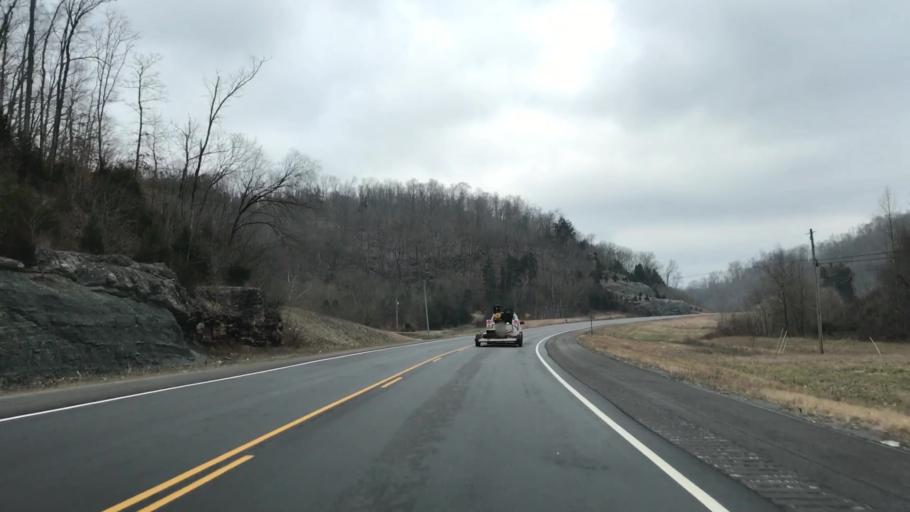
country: US
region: Kentucky
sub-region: Cumberland County
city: Burkesville
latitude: 36.9001
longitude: -85.4298
